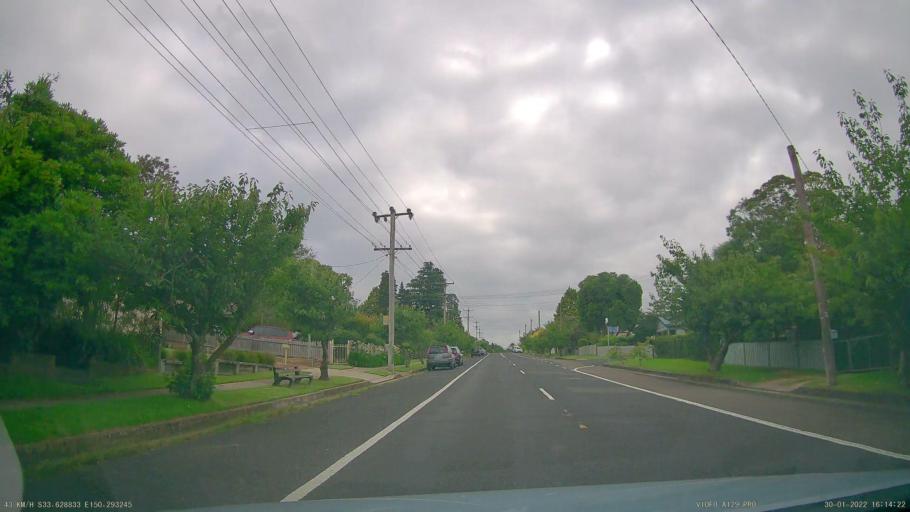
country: AU
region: New South Wales
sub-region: Blue Mountains Municipality
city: Blackheath
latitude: -33.6289
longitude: 150.2932
